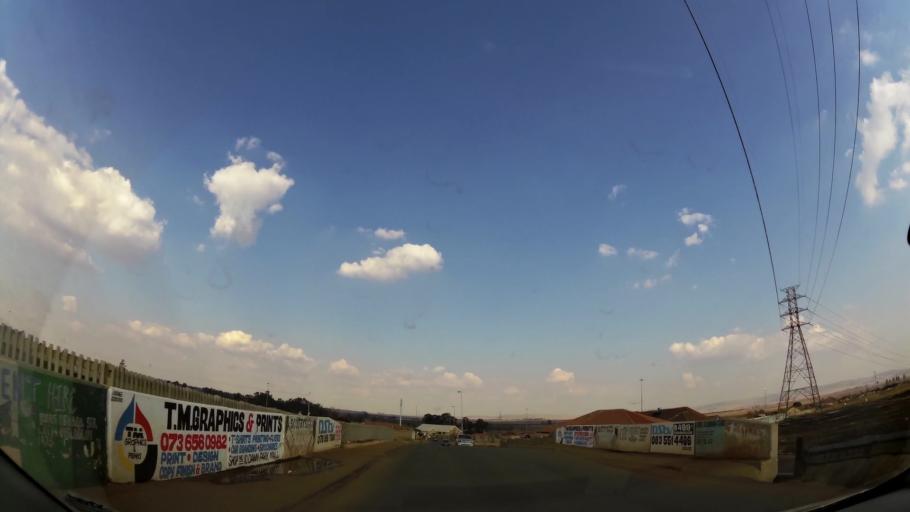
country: ZA
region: Gauteng
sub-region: Ekurhuleni Metropolitan Municipality
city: Germiston
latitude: -26.3634
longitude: 28.2278
